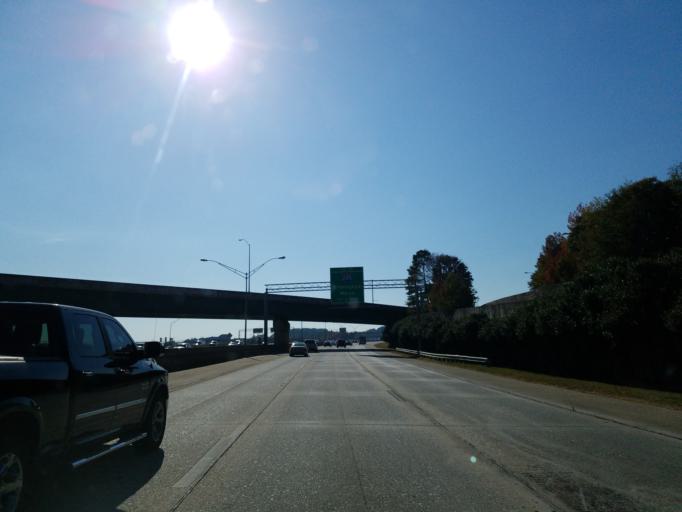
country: US
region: Georgia
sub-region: Fulton County
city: College Park
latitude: 33.6525
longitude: -84.4392
